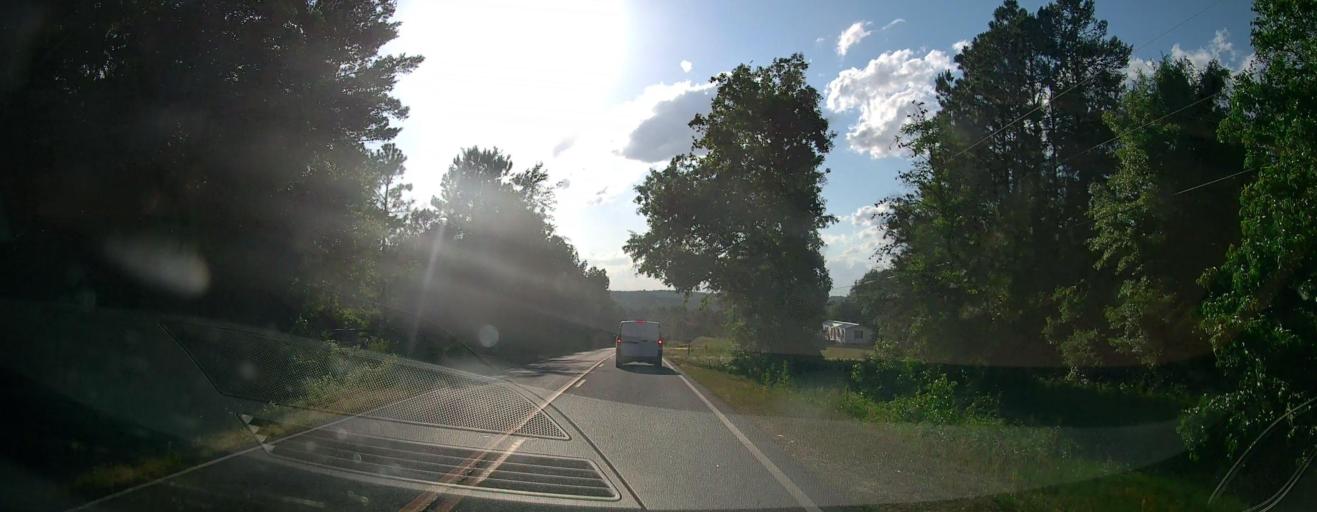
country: US
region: Georgia
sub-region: Peach County
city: Byron
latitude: 32.6761
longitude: -83.7679
